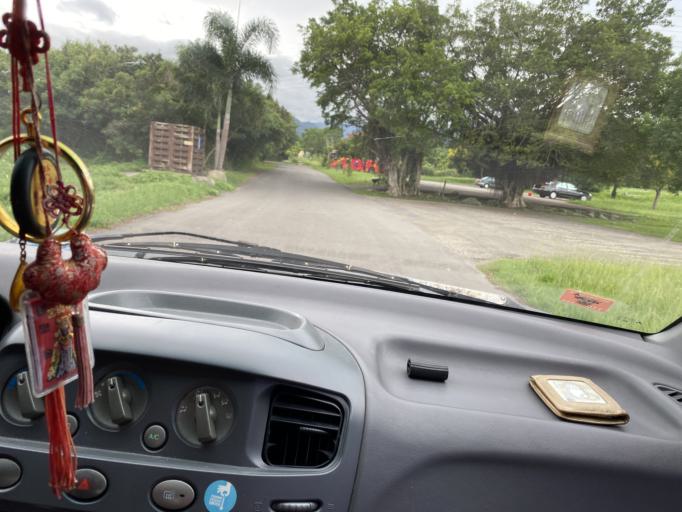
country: TW
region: Taiwan
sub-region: Hsinchu
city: Zhubei
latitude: 24.7202
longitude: 121.1030
